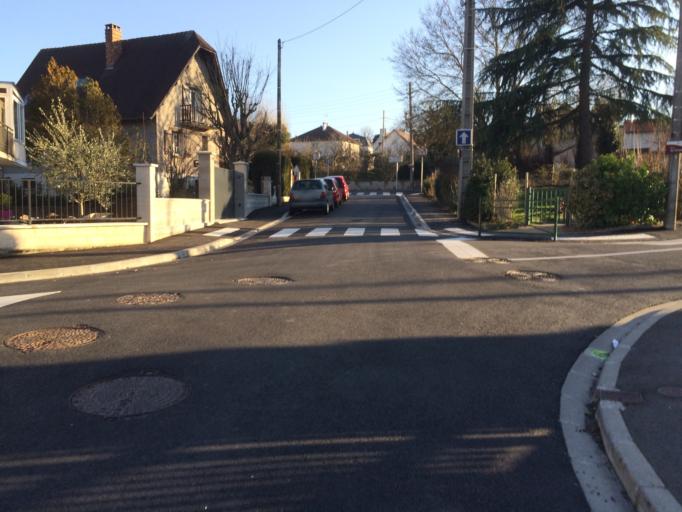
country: FR
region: Ile-de-France
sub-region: Departement de l'Essonne
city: Igny
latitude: 48.7338
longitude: 2.2182
